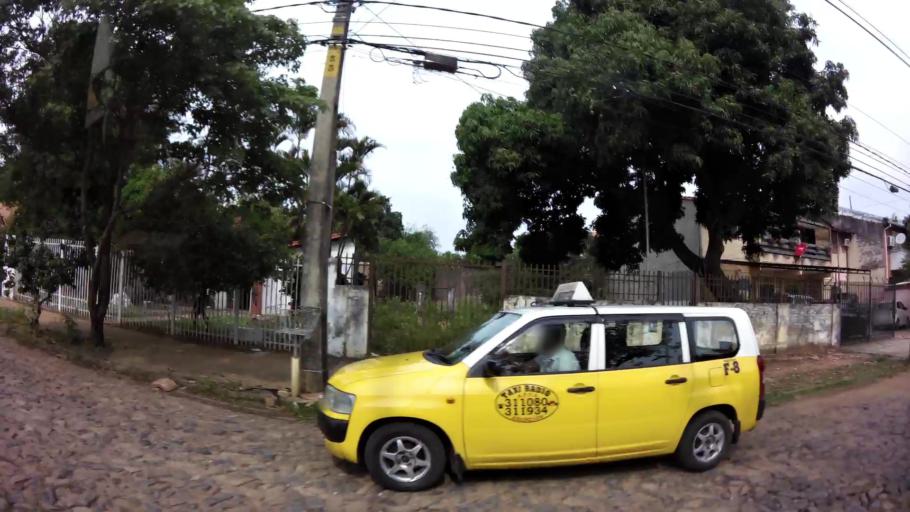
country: PY
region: Central
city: Fernando de la Mora
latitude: -25.2911
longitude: -57.5612
